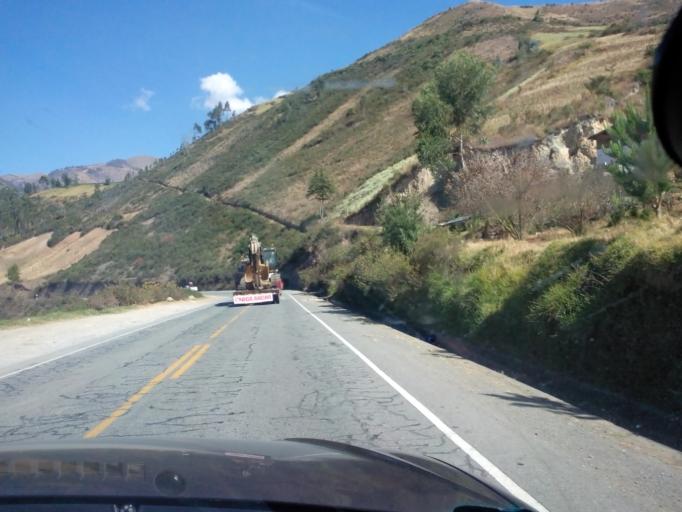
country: PE
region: Apurimac
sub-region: Provincia de Abancay
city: Cachora
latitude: -13.5523
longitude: -72.7620
